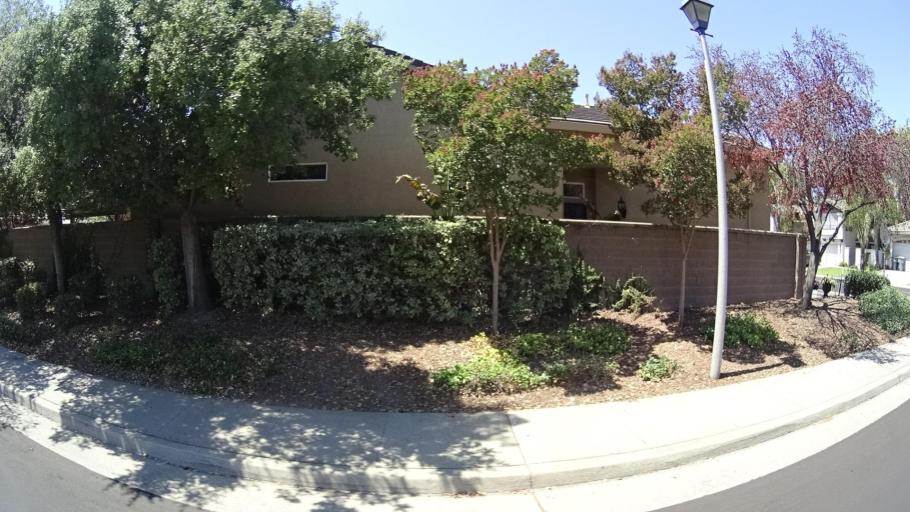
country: US
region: California
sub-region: Placer County
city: Rocklin
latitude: 38.8161
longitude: -121.2602
